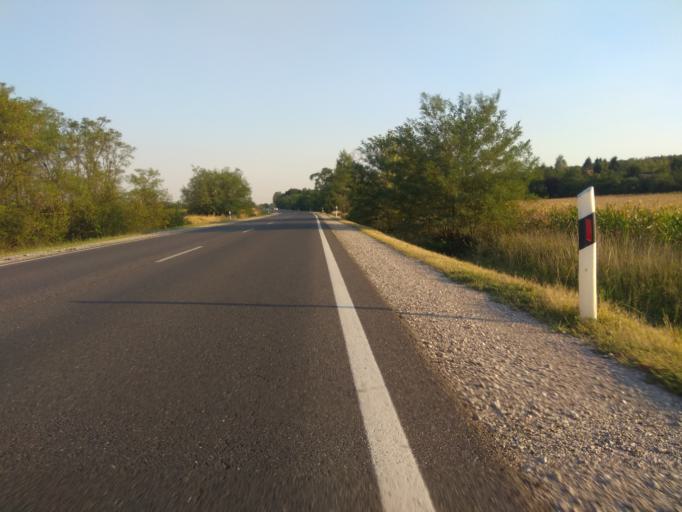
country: HU
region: Borsod-Abauj-Zemplen
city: Nyekladhaza
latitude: 47.9707
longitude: 20.8311
